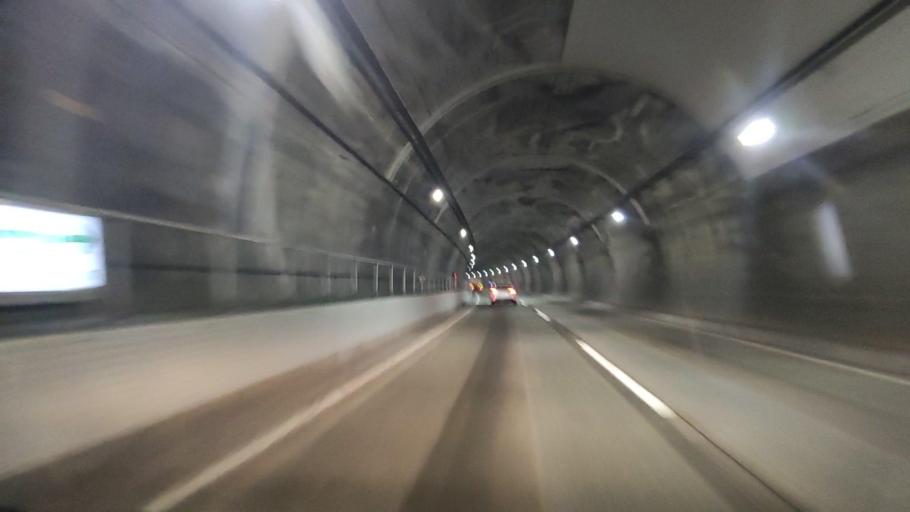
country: JP
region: Iwate
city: Ichinohe
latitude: 40.2349
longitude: 141.3942
